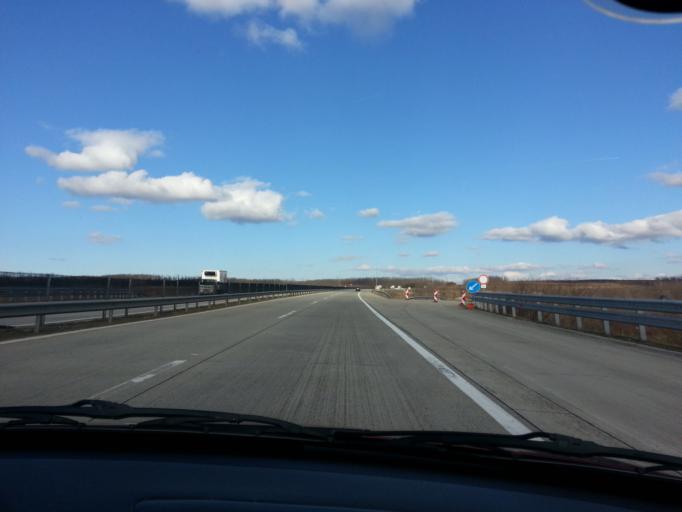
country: HU
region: Pest
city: Kerepes
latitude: 47.5541
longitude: 19.3158
